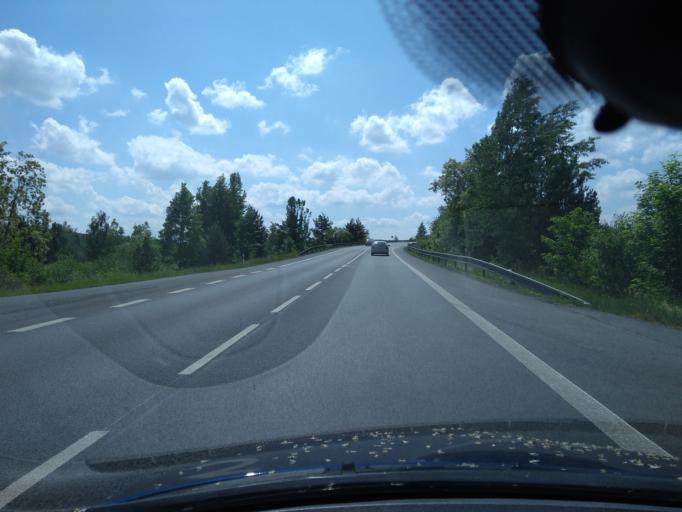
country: CZ
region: Plzensky
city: Svihov
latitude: 49.5108
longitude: 13.2986
